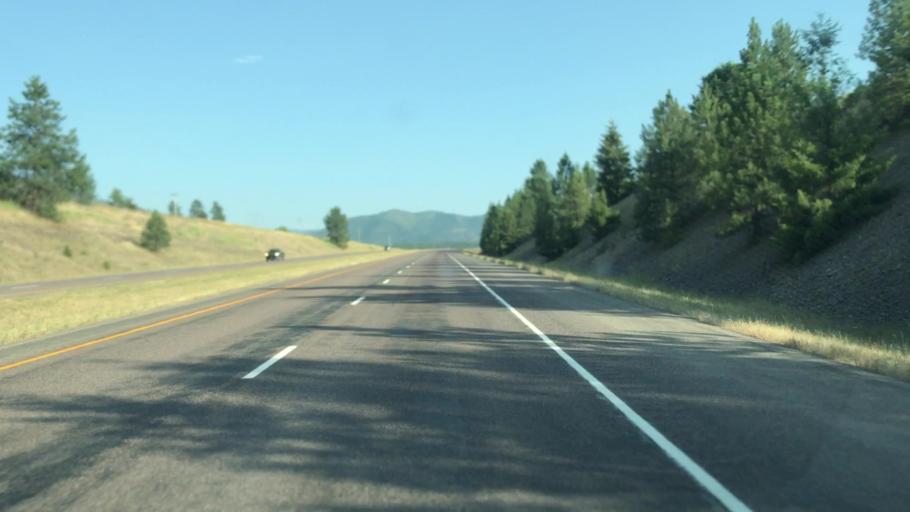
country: US
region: Montana
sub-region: Mineral County
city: Superior
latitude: 47.0505
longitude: -114.7563
